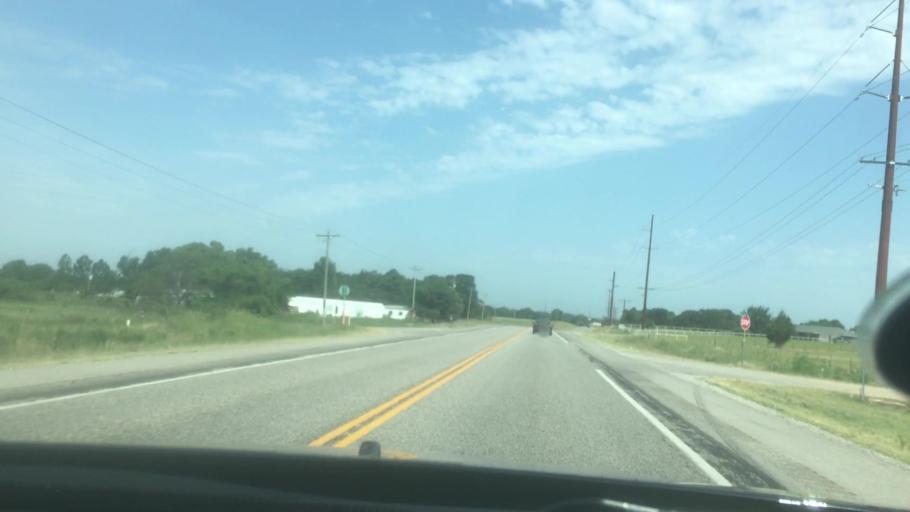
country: US
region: Oklahoma
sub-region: Seminole County
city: Konawa
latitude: 34.8540
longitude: -96.8155
